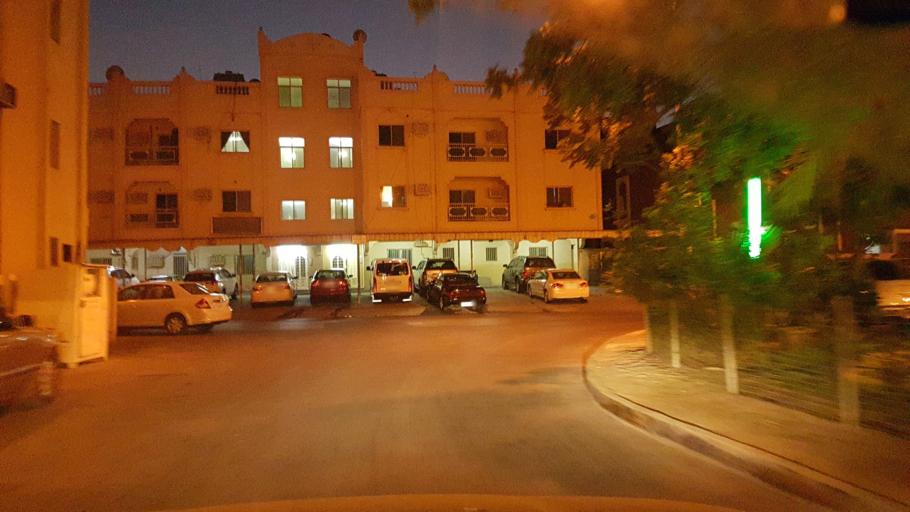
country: BH
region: Manama
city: Manama
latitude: 26.2216
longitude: 50.5803
